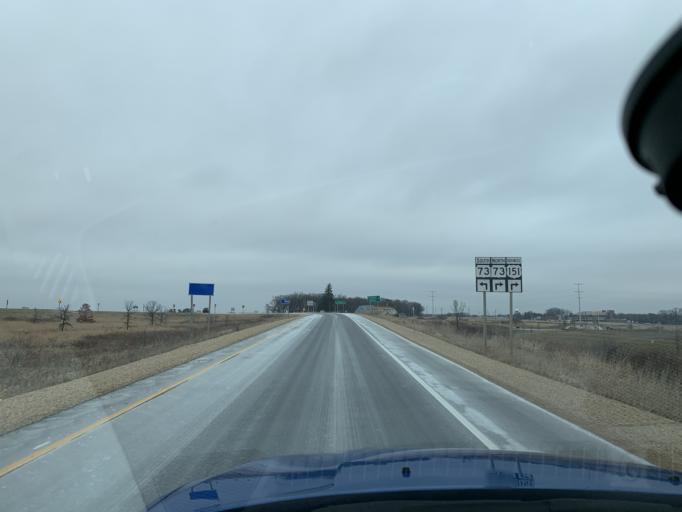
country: US
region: Wisconsin
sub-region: Columbia County
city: Columbus
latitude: 43.3163
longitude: -89.0444
